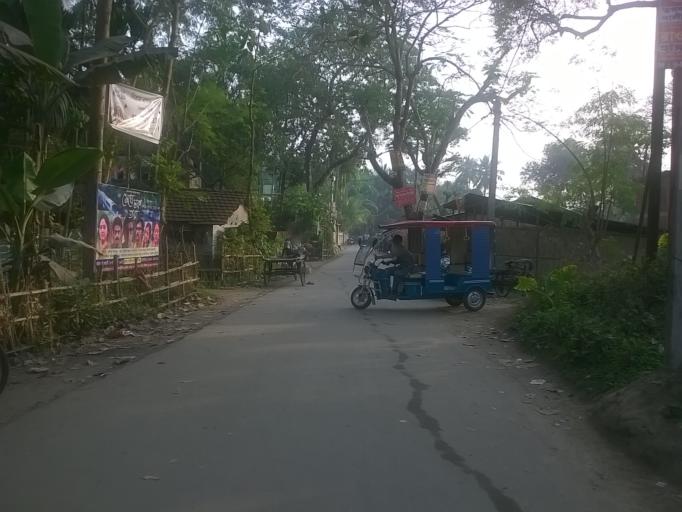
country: IN
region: West Bengal
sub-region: North 24 Parganas
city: Taki
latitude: 22.5880
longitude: 88.9162
